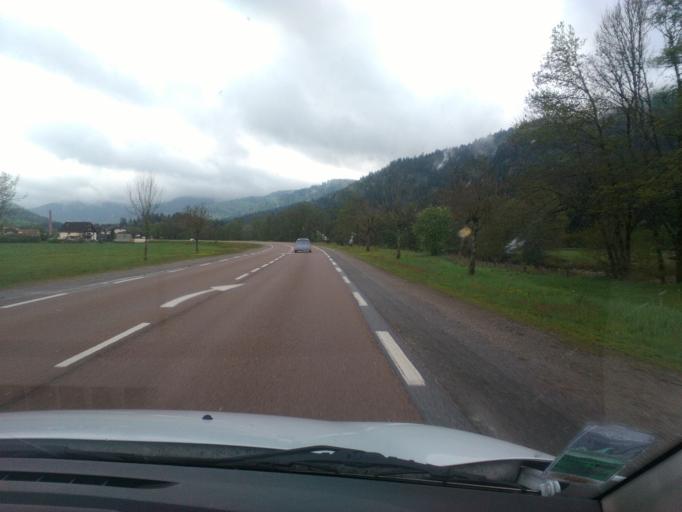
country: FR
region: Lorraine
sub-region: Departement des Vosges
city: Vagney
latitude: 47.9992
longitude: 6.7118
